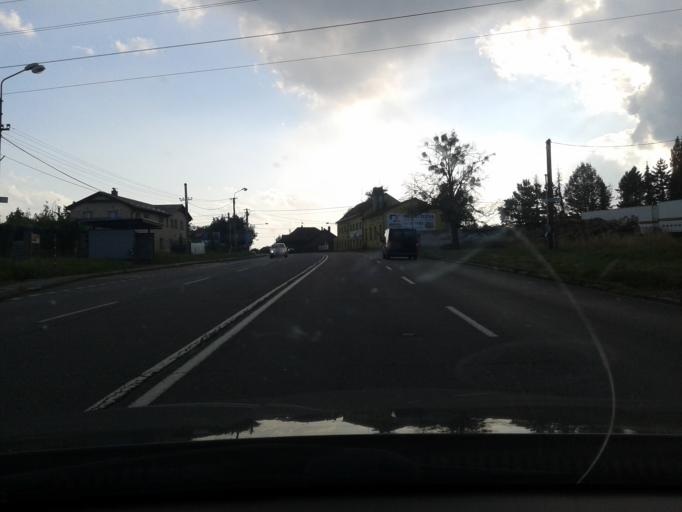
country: CZ
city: Petrvald
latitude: 49.8273
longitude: 18.3739
